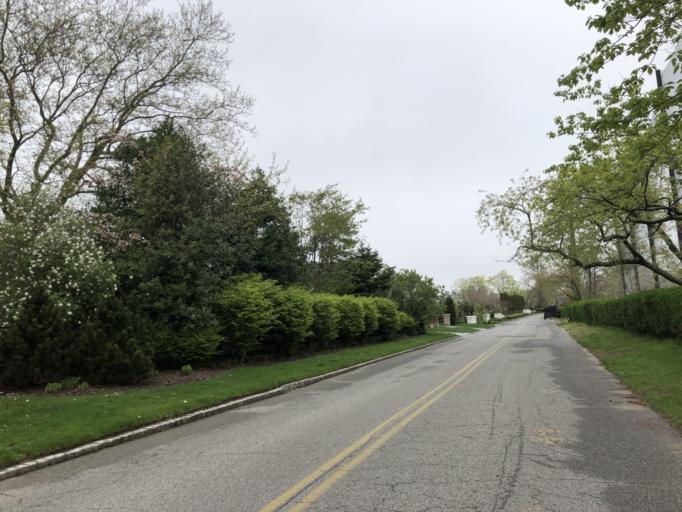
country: US
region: New York
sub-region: Nassau County
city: Hewlett Harbor
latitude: 40.6309
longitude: -73.6893
